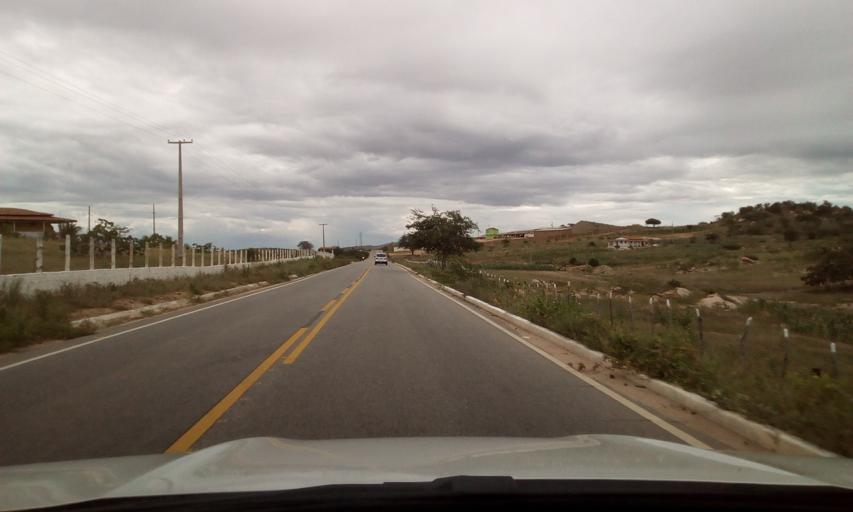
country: BR
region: Paraiba
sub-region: Picui
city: Picui
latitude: -6.5488
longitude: -36.2976
